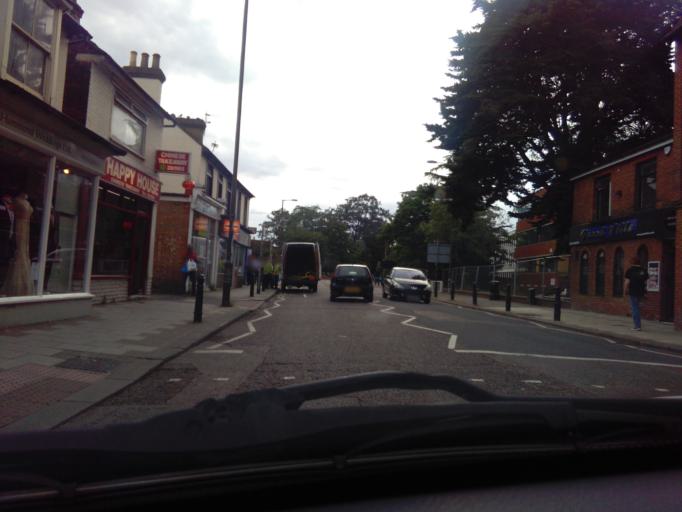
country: GB
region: England
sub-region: Bedford
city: Bedford
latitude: 52.1394
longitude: -0.4756
